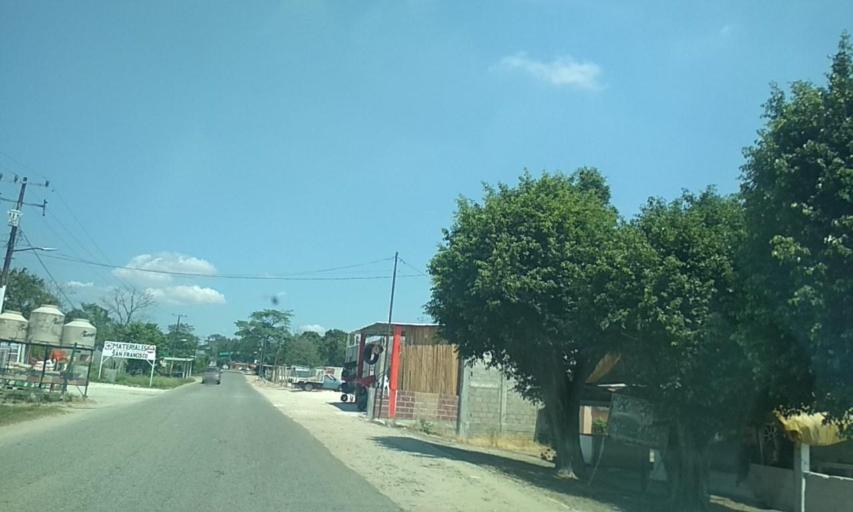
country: MX
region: Tabasco
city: Huimanguillo
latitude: 17.7919
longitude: -93.4402
